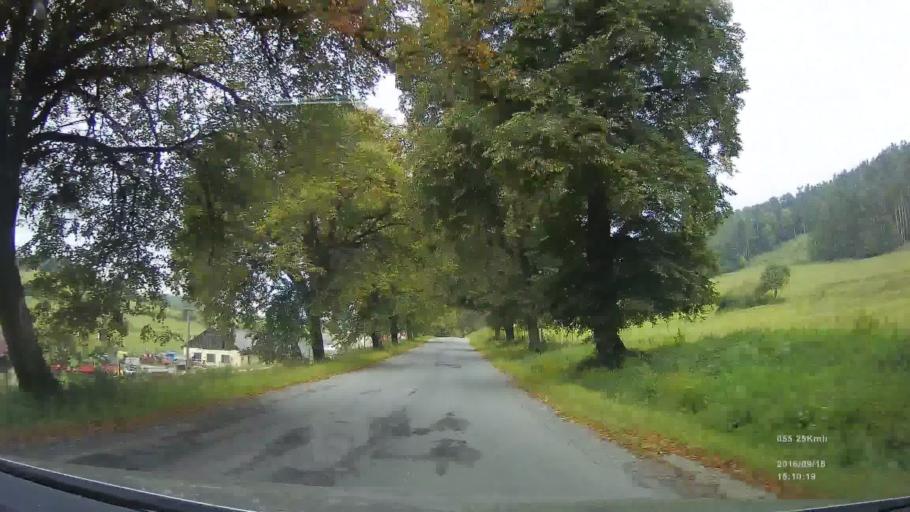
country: SK
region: Presovsky
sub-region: Okres Presov
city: Levoca
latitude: 49.0185
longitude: 20.5006
